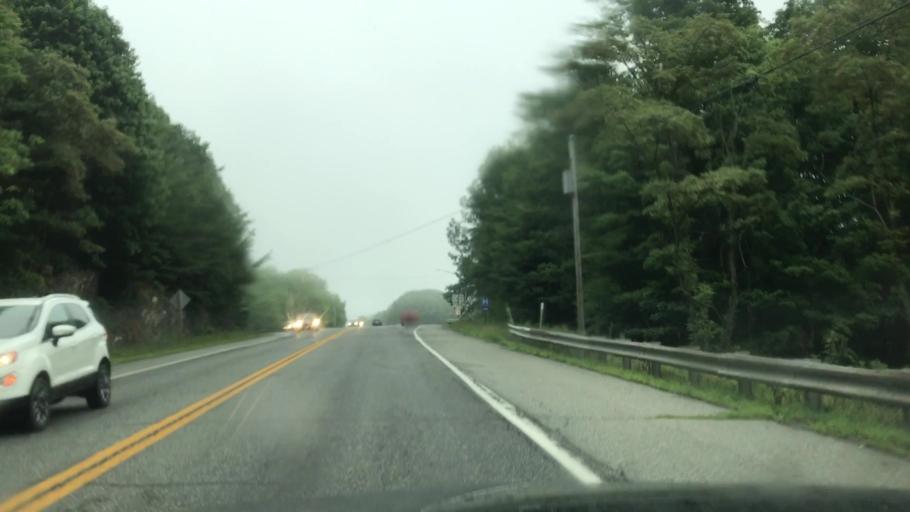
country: US
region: Maine
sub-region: Lincoln County
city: Damariscotta
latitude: 44.0306
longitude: -69.5456
